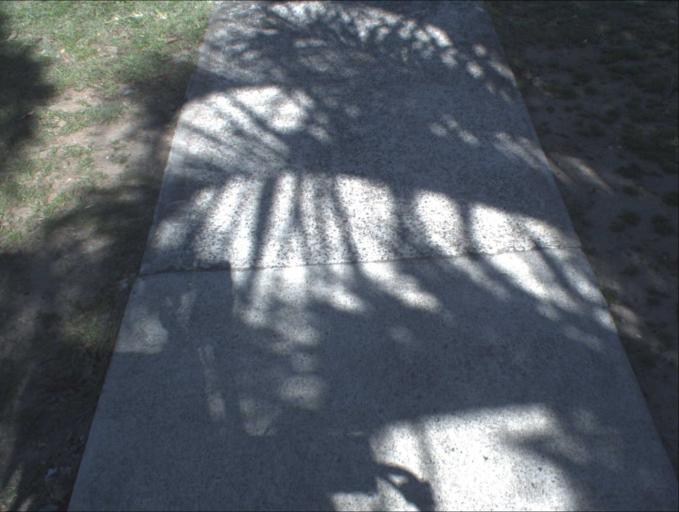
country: AU
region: Queensland
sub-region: Logan
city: Beenleigh
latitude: -27.7091
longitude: 153.1676
